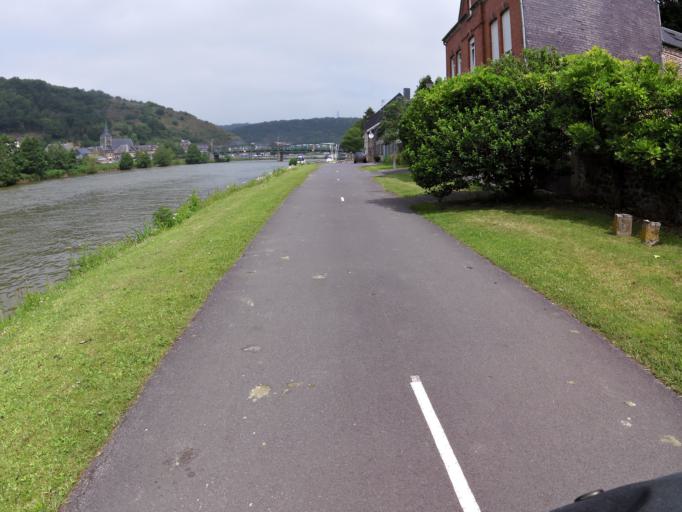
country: FR
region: Champagne-Ardenne
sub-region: Departement des Ardennes
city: Vireux-Wallerand
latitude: 50.0825
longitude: 4.7270
